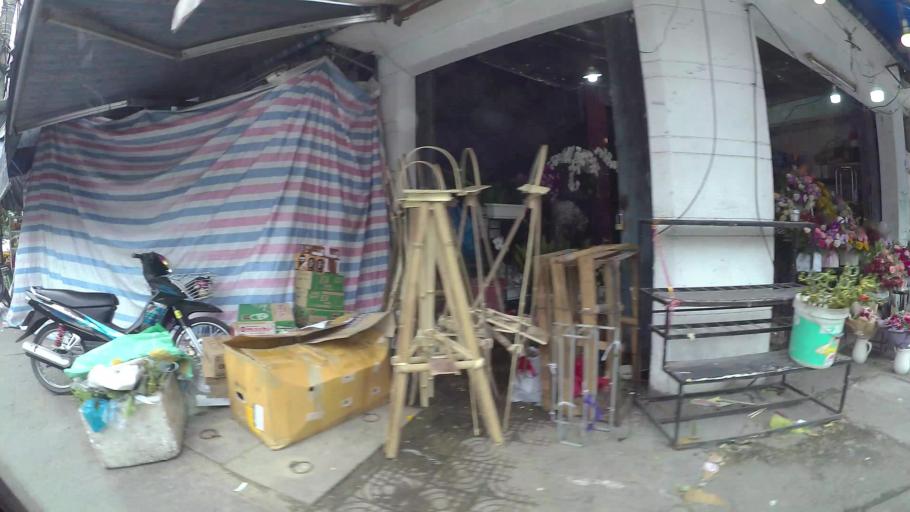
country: VN
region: Da Nang
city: Da Nang
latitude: 16.0528
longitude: 108.2175
